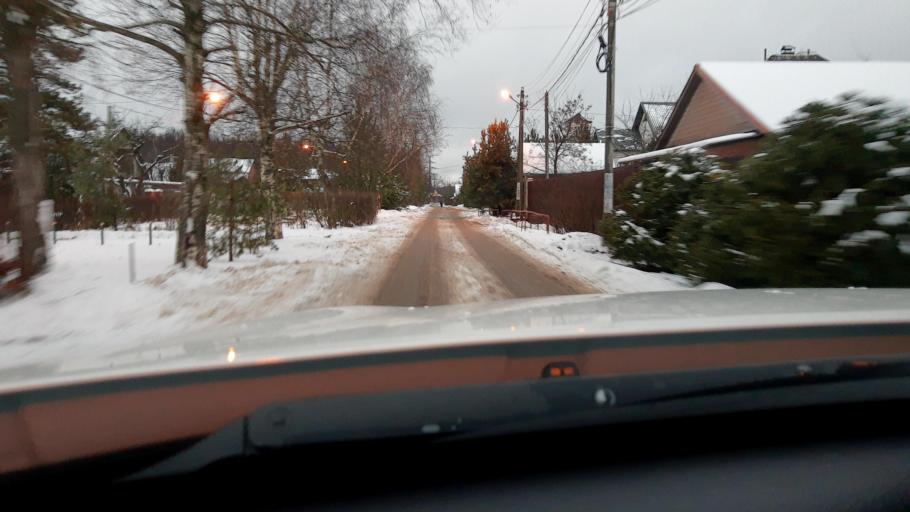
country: RU
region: Moskovskaya
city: Krasnogorsk
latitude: 55.8651
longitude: 37.3143
